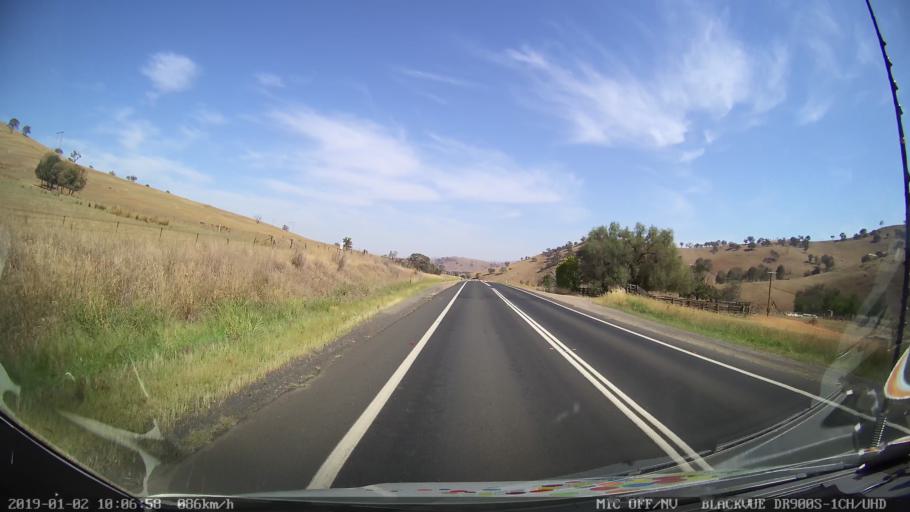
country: AU
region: New South Wales
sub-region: Gundagai
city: Gundagai
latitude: -35.1431
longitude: 148.1172
